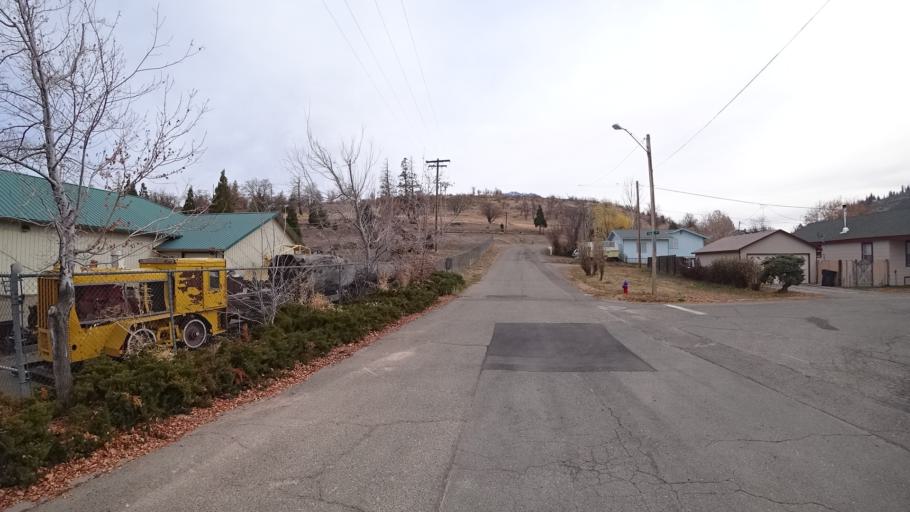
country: US
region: California
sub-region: Siskiyou County
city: Weed
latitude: 41.4251
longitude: -122.3835
